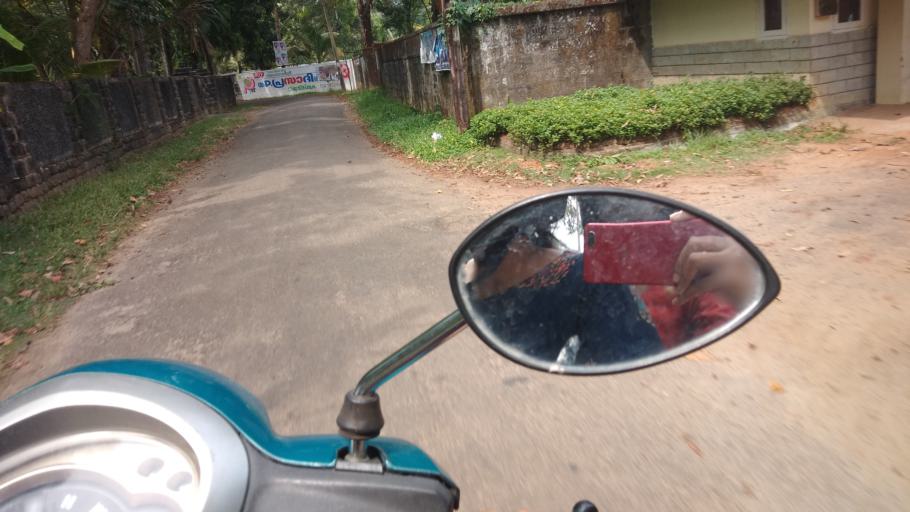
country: IN
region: Kerala
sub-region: Alappuzha
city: Shertallai
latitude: 9.6065
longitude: 76.3636
